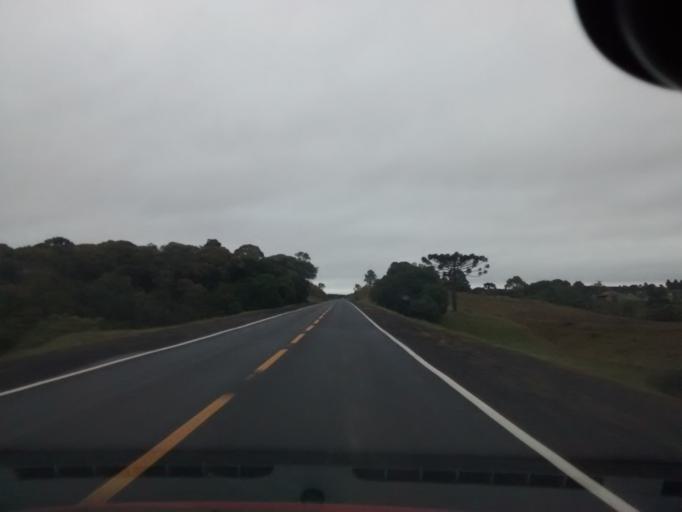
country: BR
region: Rio Grande do Sul
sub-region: Vacaria
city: Estrela
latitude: -28.1537
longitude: -50.6648
